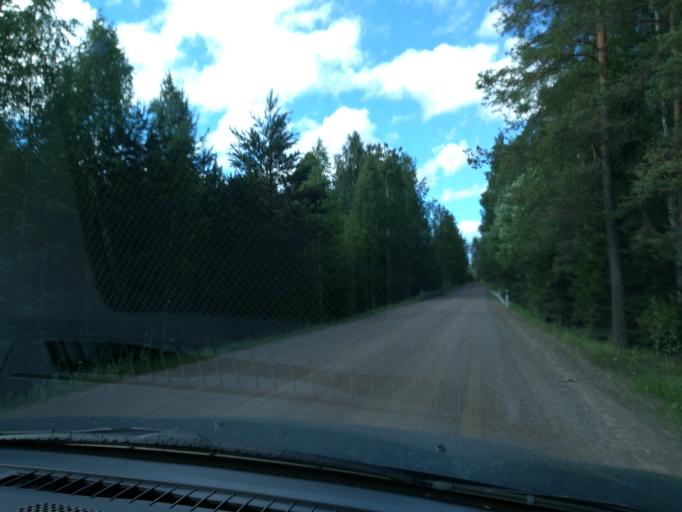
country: FI
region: South Karelia
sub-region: Lappeenranta
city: Savitaipale
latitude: 61.2910
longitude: 27.6573
